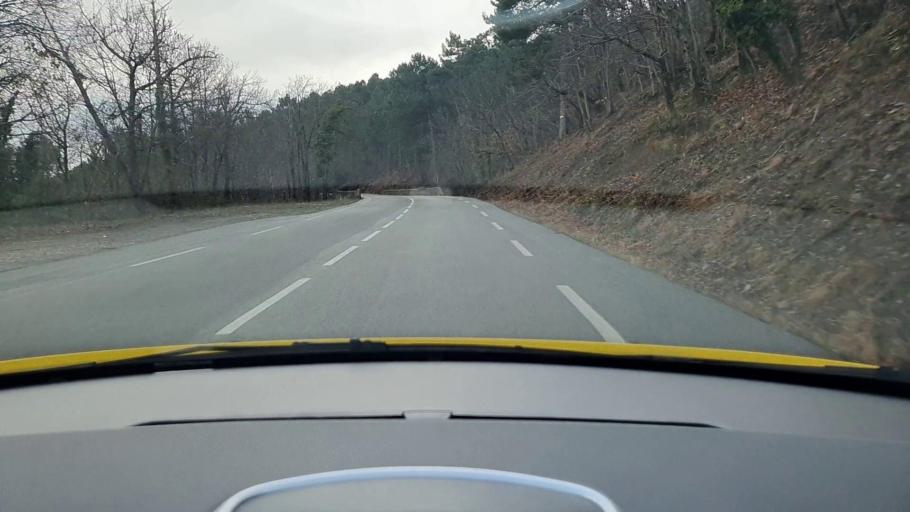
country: FR
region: Languedoc-Roussillon
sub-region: Departement du Gard
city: Branoux-les-Taillades
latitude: 44.2748
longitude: 4.0113
